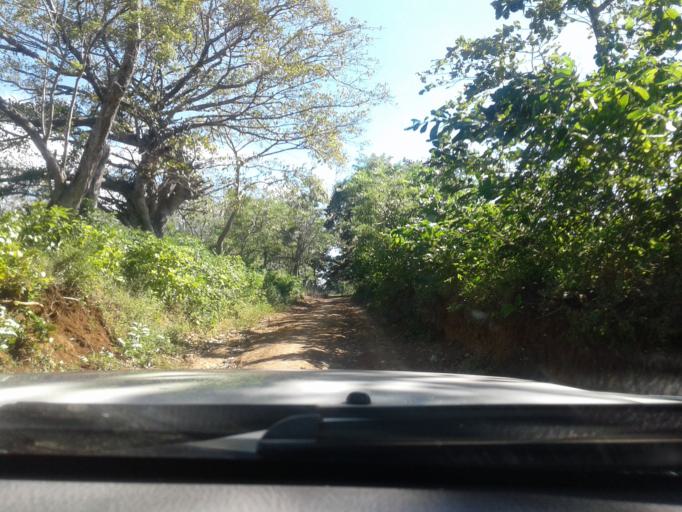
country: NI
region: Carazo
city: Santa Teresa
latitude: 11.7394
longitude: -86.1866
